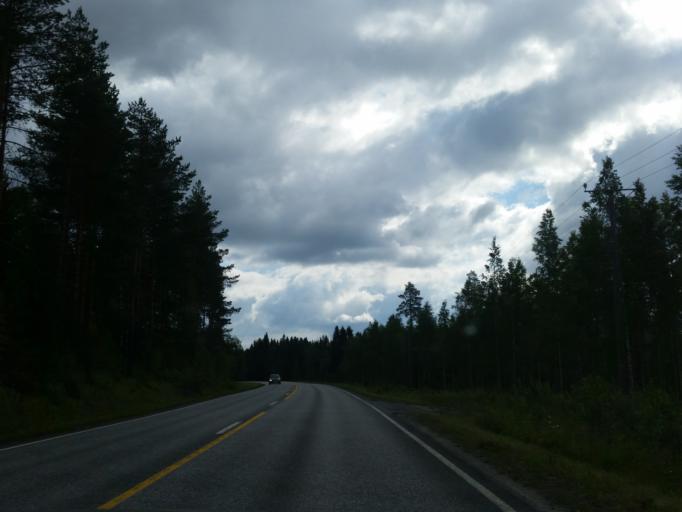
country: FI
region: Northern Savo
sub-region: Kuopio
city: Kuopio
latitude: 62.8410
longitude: 27.5000
